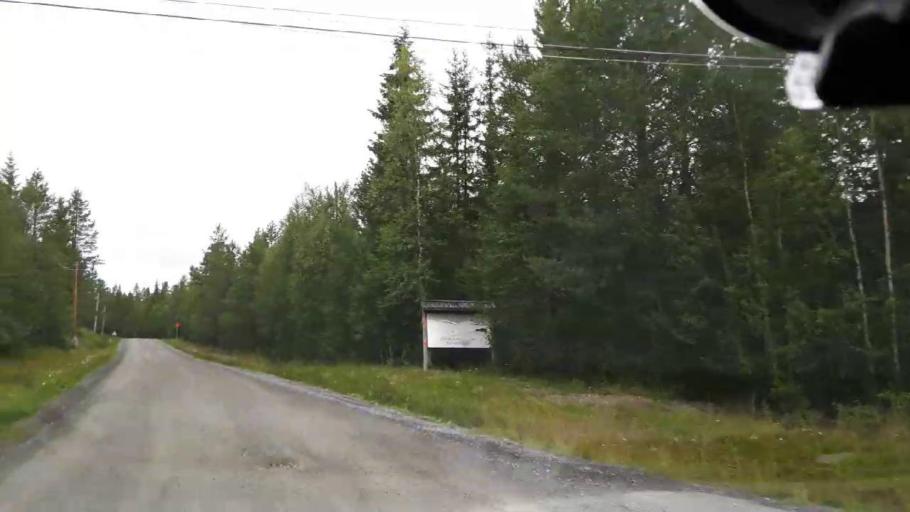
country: SE
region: Jaemtland
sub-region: Krokoms Kommun
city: Valla
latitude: 63.6836
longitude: 13.8803
